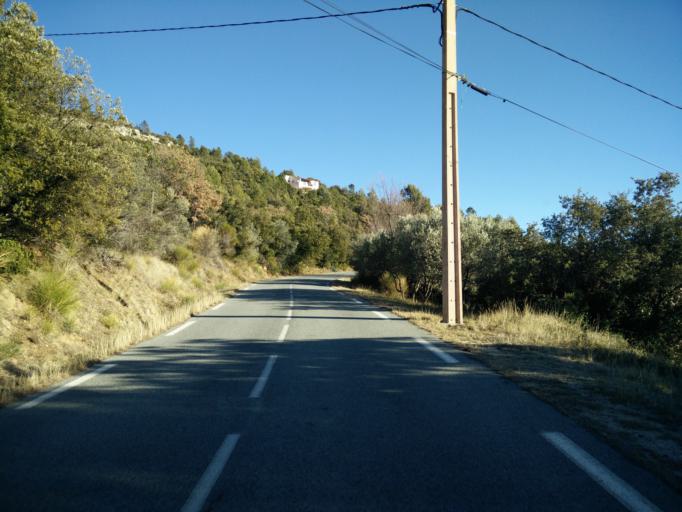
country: FR
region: Provence-Alpes-Cote d'Azur
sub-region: Departement du Var
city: Villecroze
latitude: 43.5939
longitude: 6.2886
